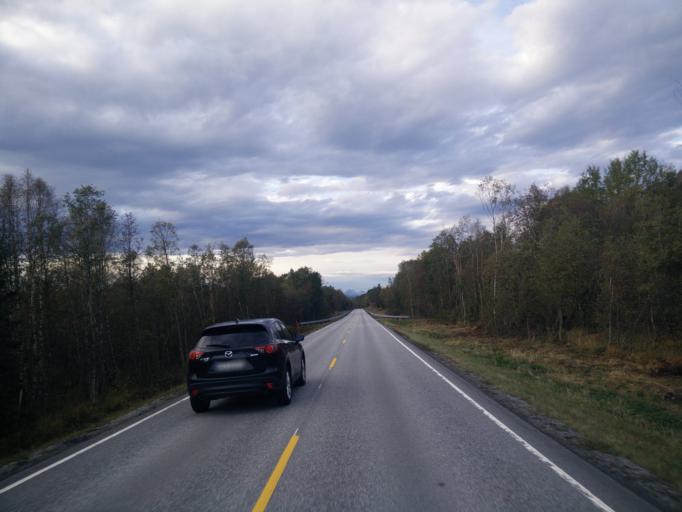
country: NO
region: More og Romsdal
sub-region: Molde
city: Hjelset
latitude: 62.7957
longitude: 7.5460
